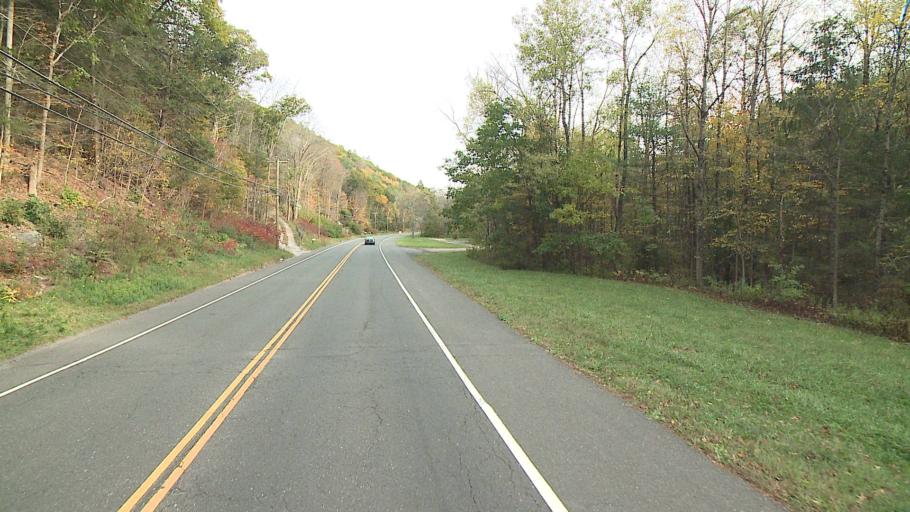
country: US
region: Connecticut
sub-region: Litchfield County
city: Canaan
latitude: 42.0016
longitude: -73.2203
